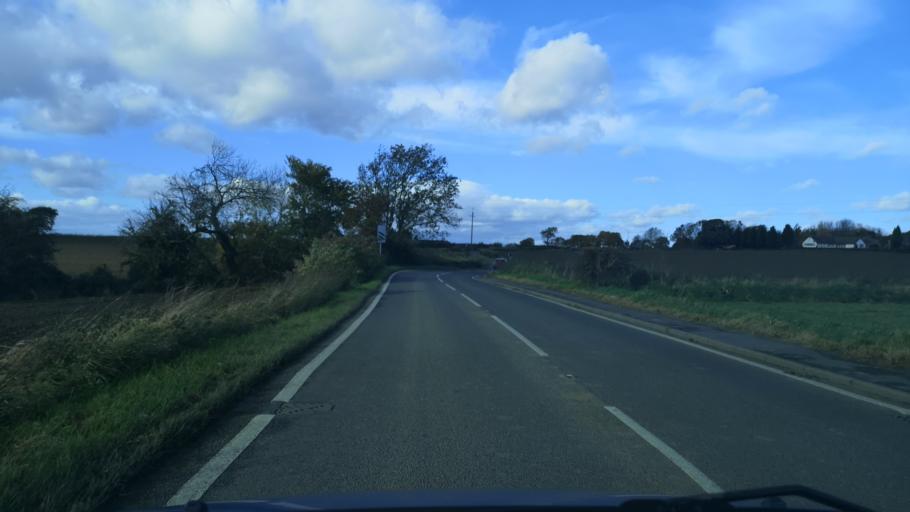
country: GB
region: England
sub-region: City and Borough of Wakefield
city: Featherstone
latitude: 53.6651
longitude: -1.3501
